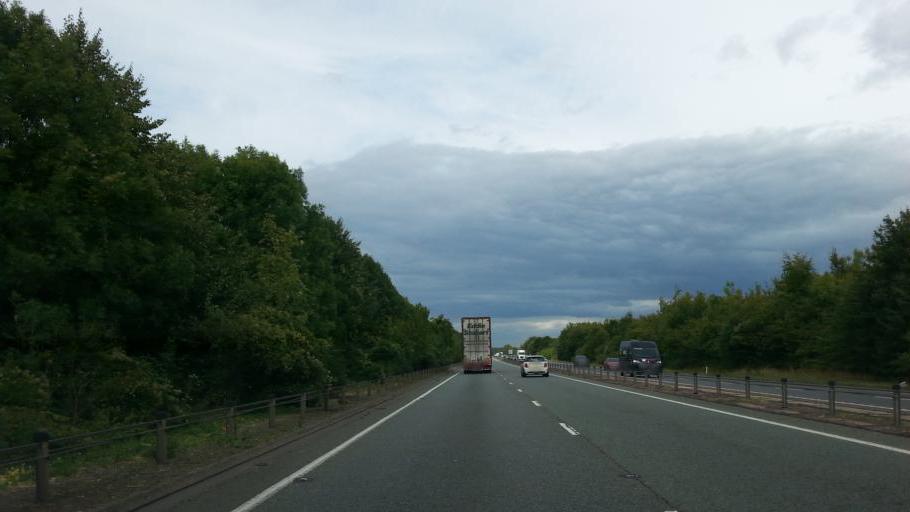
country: GB
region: England
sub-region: Cambridgeshire
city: Sawston
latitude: 52.0988
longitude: 0.2066
